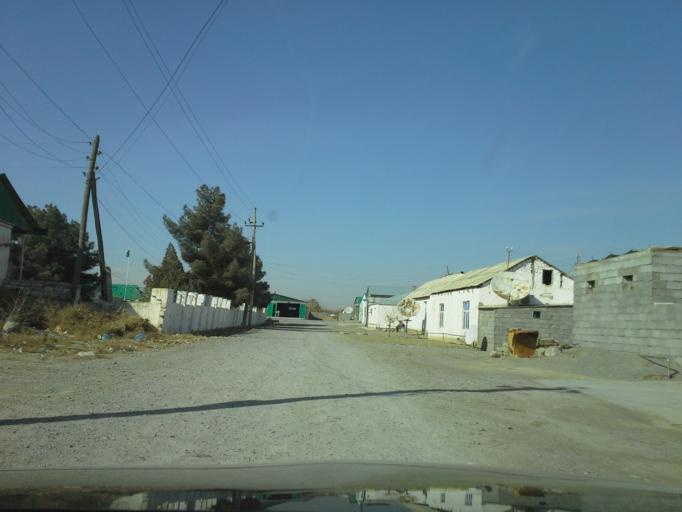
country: TM
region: Ahal
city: Abadan
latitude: 38.1120
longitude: 58.0356
